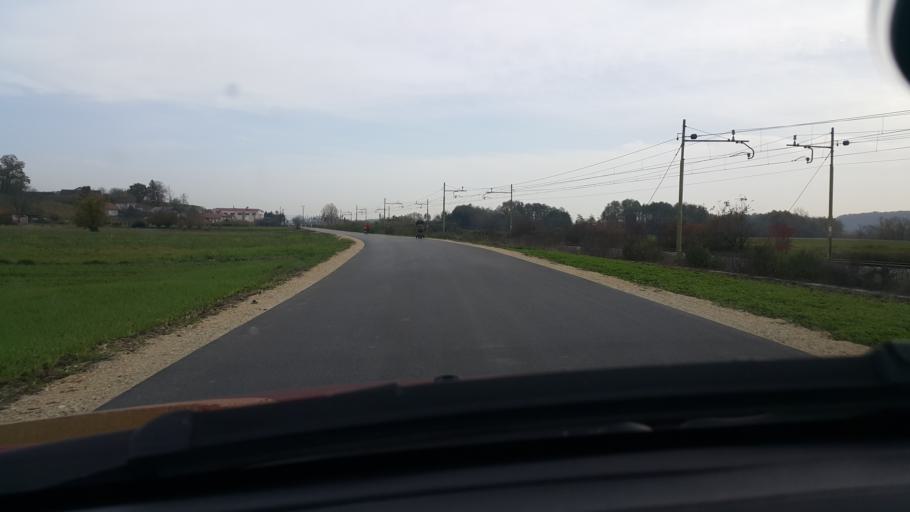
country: SI
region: Brezice
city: Brezice
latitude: 45.9043
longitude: 15.6368
